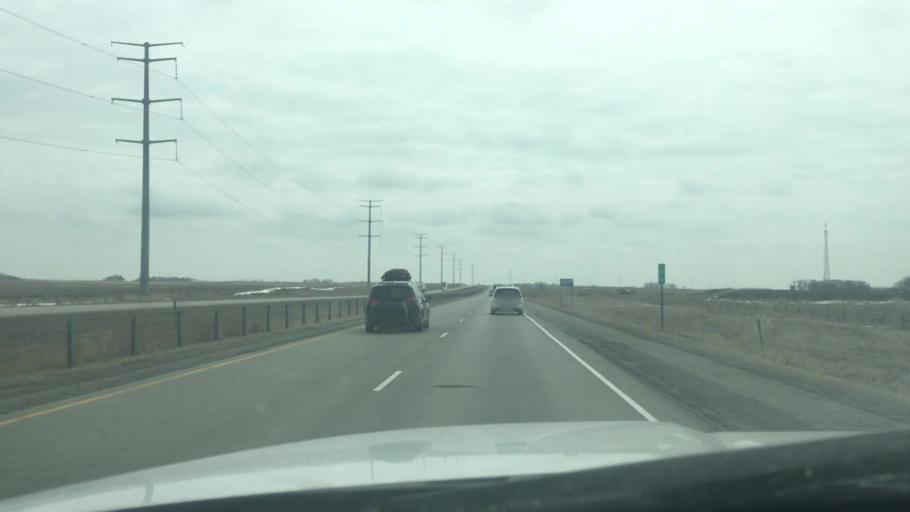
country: US
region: Minnesota
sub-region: Clay County
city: Barnesville
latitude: 46.5398
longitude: -96.3032
